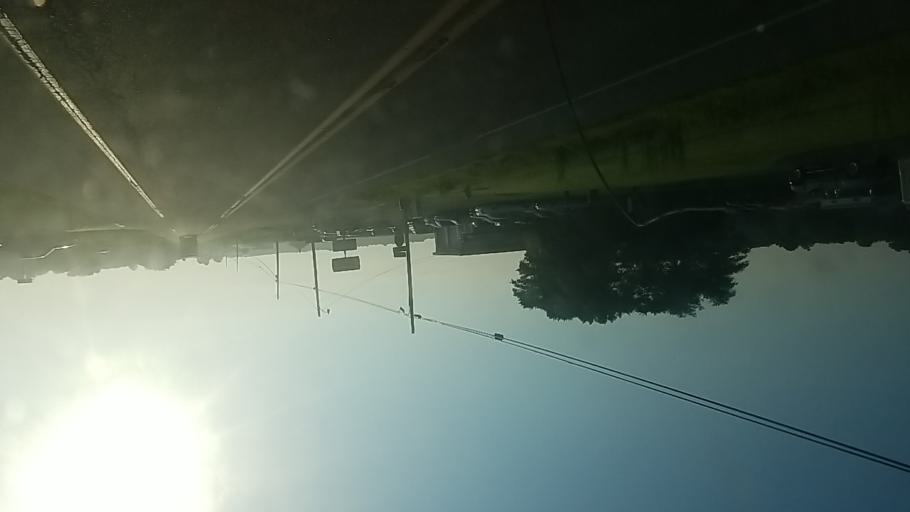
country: US
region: Delaware
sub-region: Sussex County
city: Selbyville
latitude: 38.4639
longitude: -75.1790
